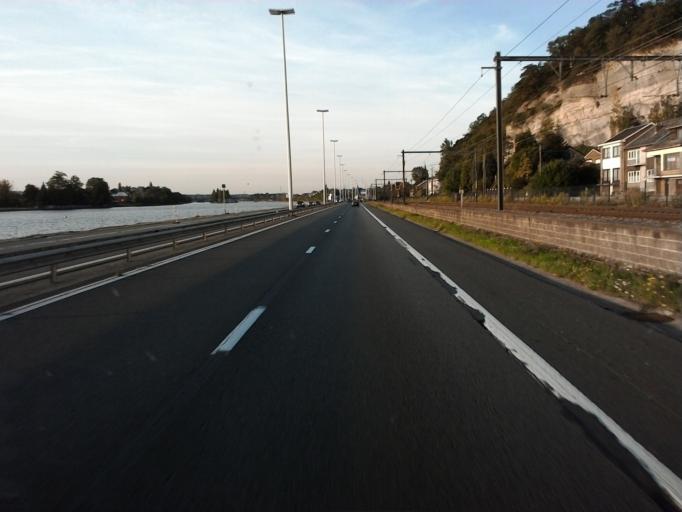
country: BE
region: Wallonia
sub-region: Province de Liege
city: Vise
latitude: 50.7249
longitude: 5.6928
